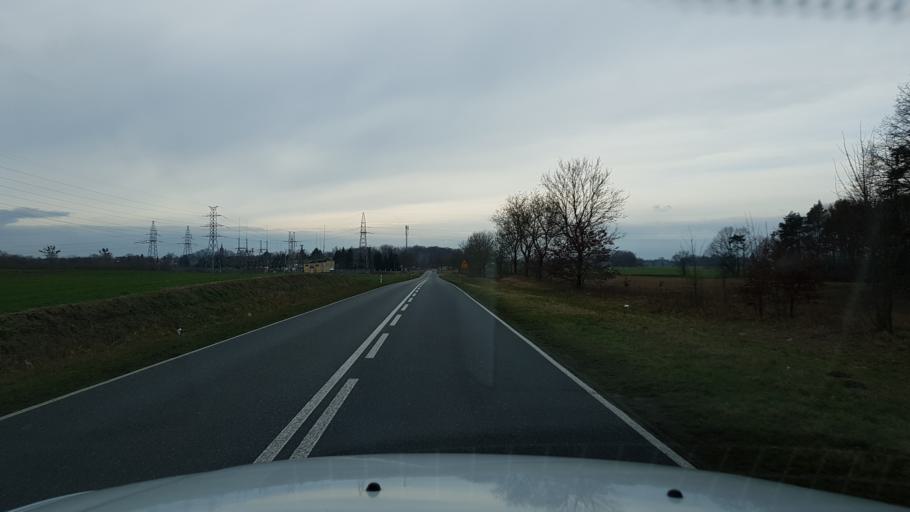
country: PL
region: West Pomeranian Voivodeship
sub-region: Powiat mysliborski
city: Nowogrodek Pomorski
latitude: 52.9965
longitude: 15.0732
